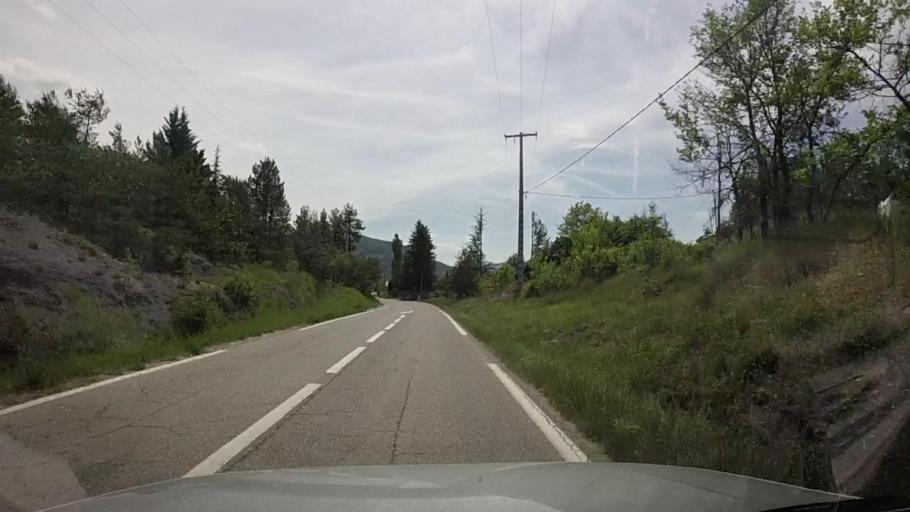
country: FR
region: Provence-Alpes-Cote d'Azur
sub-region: Departement des Alpes-de-Haute-Provence
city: Le Brusquet
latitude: 44.1510
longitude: 6.2962
